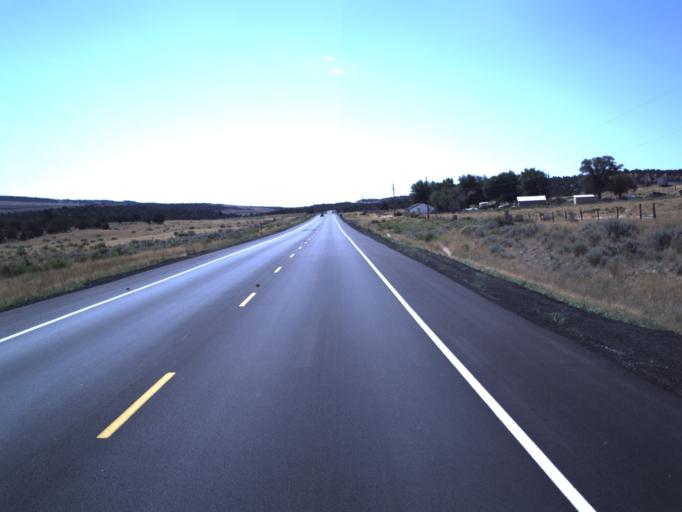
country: US
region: Utah
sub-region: Utah County
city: Eagle Mountain
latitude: 40.0283
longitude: -112.2829
